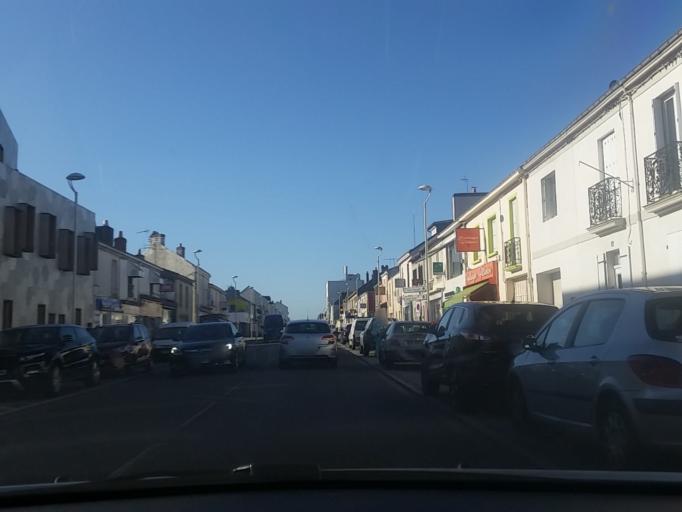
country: FR
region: Pays de la Loire
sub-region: Departement de la Loire-Atlantique
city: Reze
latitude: 47.1831
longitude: -1.5459
